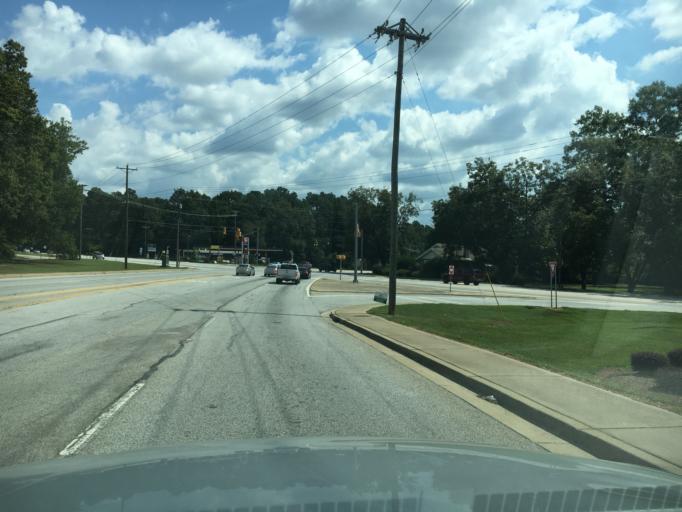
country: US
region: South Carolina
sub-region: Greenwood County
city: Greenwood
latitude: 34.1951
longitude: -82.1900
